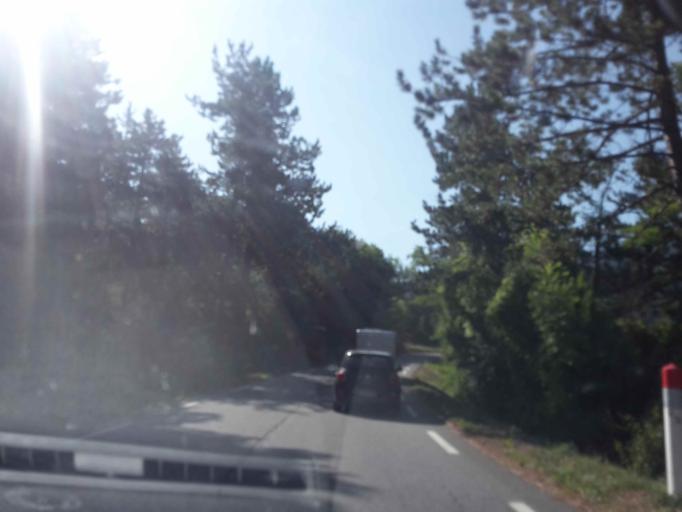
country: FR
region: Provence-Alpes-Cote d'Azur
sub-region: Departement des Hautes-Alpes
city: Guillestre
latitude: 44.6526
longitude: 6.6500
